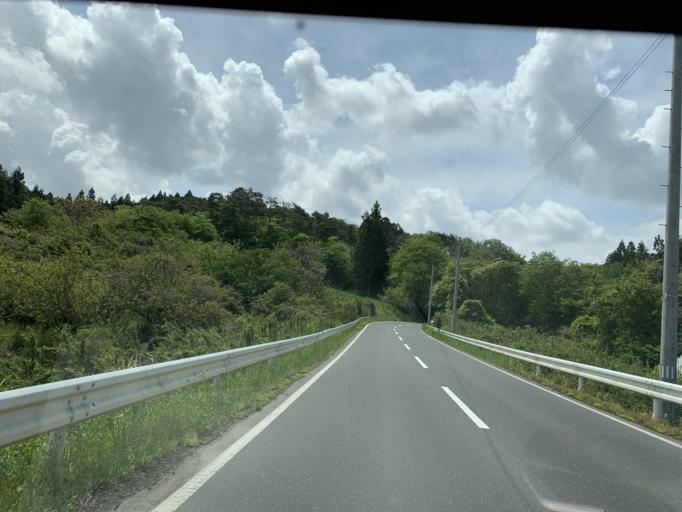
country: JP
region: Iwate
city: Ichinoseki
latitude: 38.7859
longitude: 141.0009
